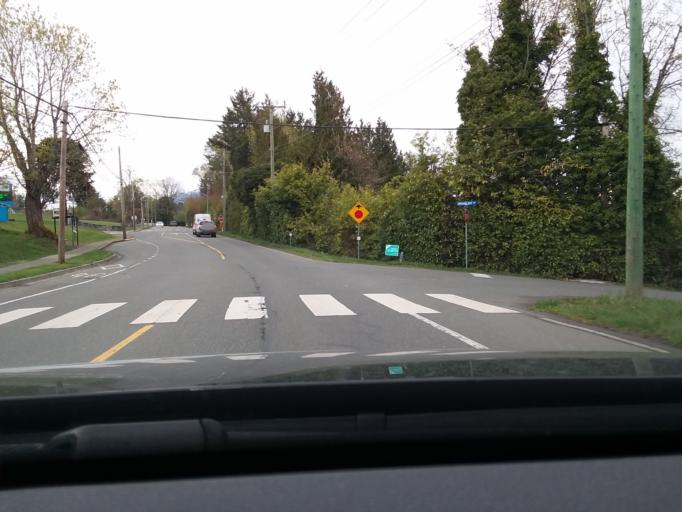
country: CA
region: British Columbia
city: North Saanich
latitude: 48.6245
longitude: -123.4185
